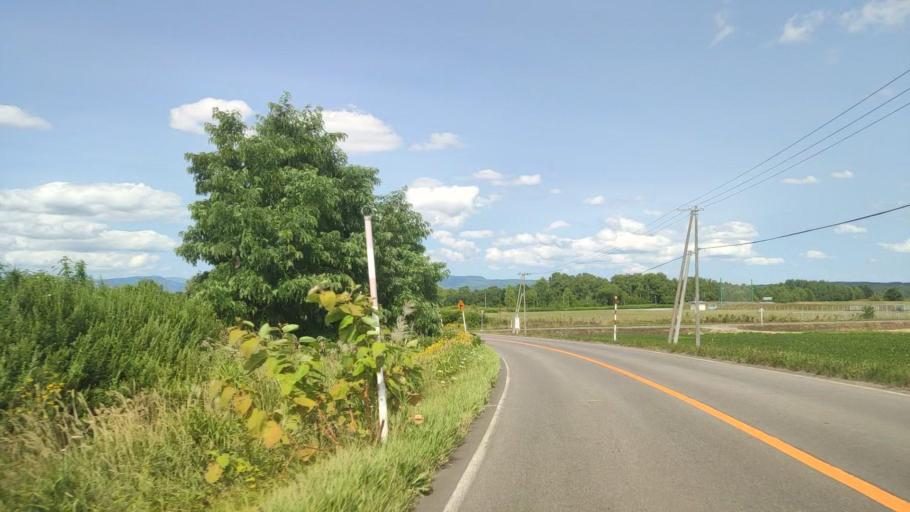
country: JP
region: Hokkaido
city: Nayoro
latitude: 44.2824
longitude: 142.4282
